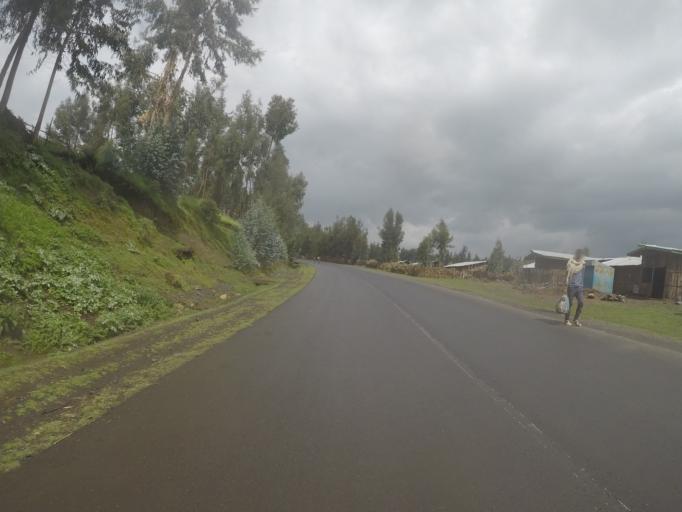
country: ET
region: Amhara
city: Debark'
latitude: 13.1177
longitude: 37.8775
